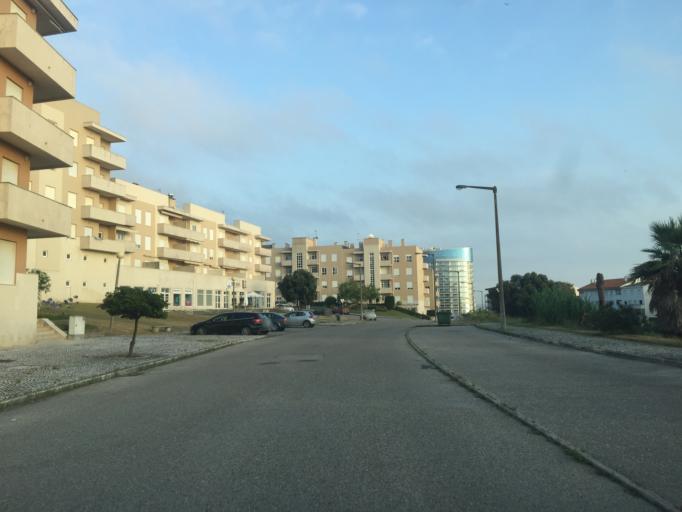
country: PT
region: Coimbra
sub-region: Figueira da Foz
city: Figueira da Foz
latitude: 40.1594
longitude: -8.8679
